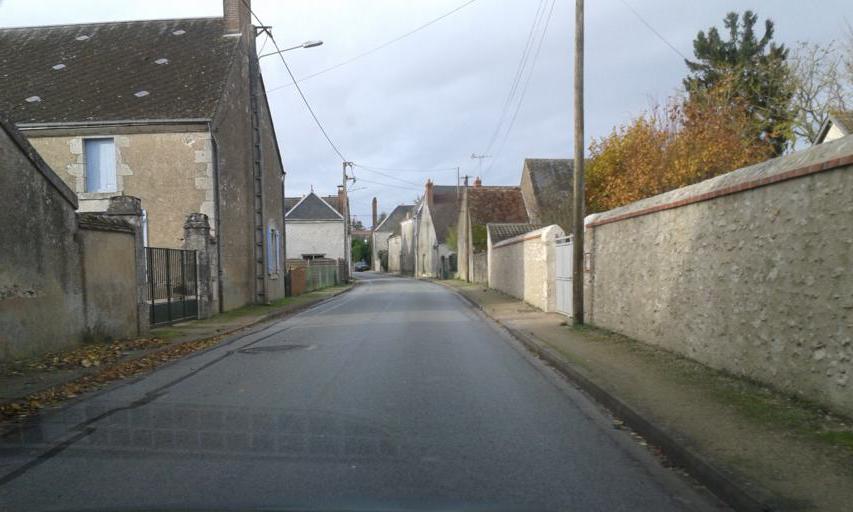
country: FR
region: Centre
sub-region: Departement du Loiret
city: Beaugency
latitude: 47.8051
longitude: 1.6406
